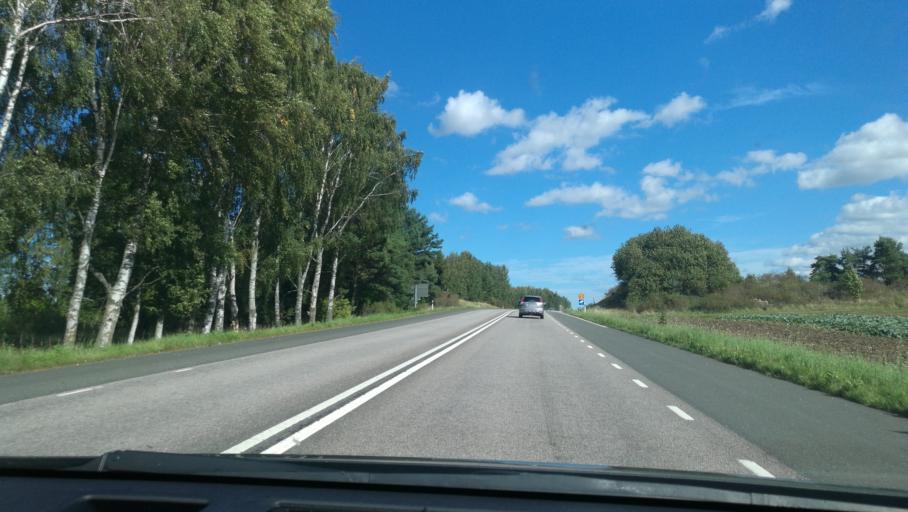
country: SE
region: Vaestra Goetaland
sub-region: Gotene Kommun
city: Kallby
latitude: 58.5021
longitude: 13.3069
